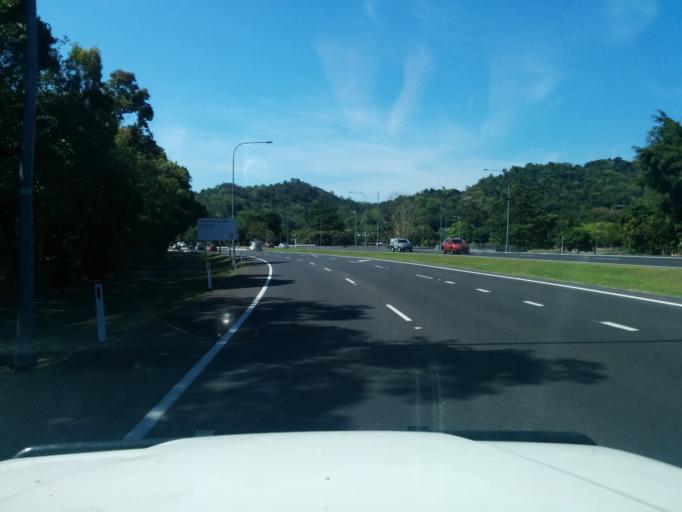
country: AU
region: Queensland
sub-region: Cairns
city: Redlynch
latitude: -16.8981
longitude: 145.7095
